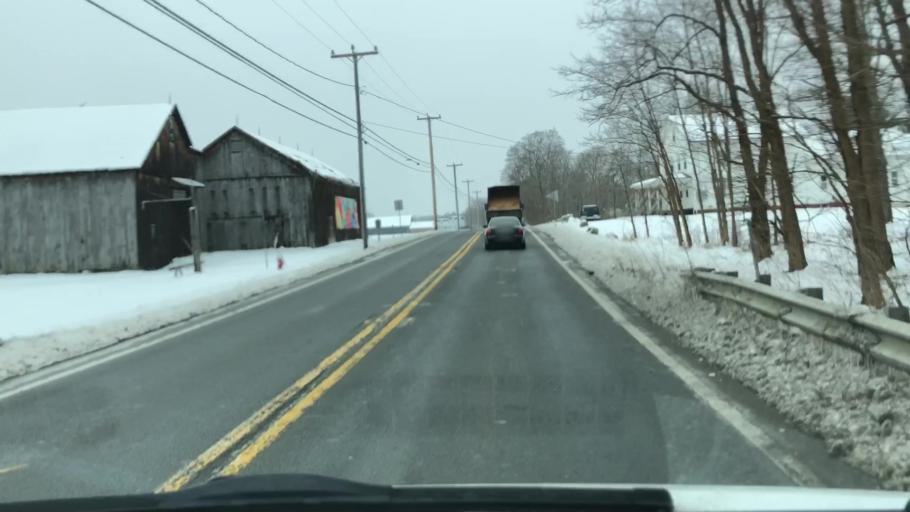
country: US
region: Massachusetts
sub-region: Franklin County
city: Whately
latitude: 42.4074
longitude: -72.6239
